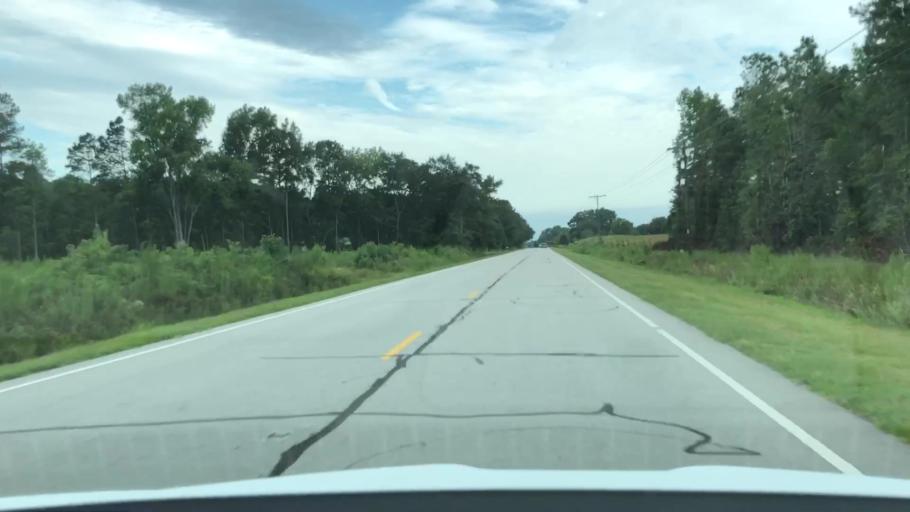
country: US
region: North Carolina
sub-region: Lenoir County
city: Kinston
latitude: 35.1309
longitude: -77.5242
